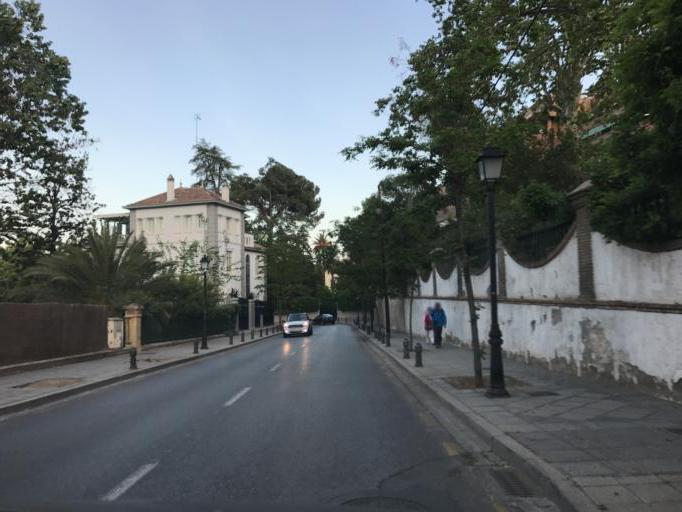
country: ES
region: Andalusia
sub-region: Provincia de Granada
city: Granada
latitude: 37.1692
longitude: -3.5901
